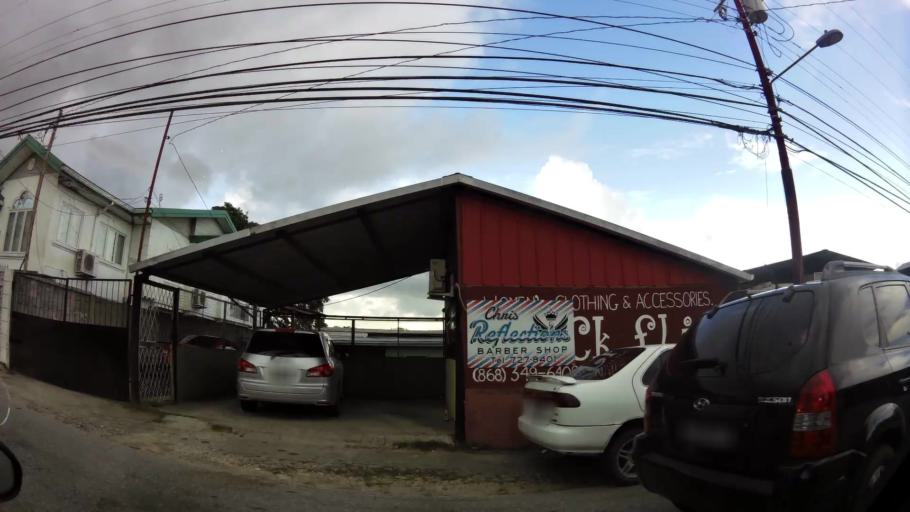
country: TT
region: City of San Fernando
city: Mon Repos
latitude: 10.2448
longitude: -61.4499
